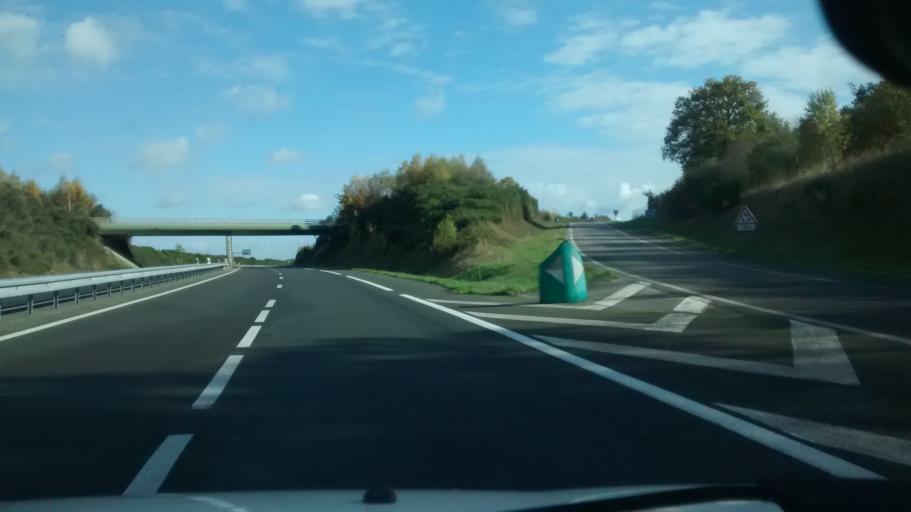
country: FR
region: Pays de la Loire
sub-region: Departement de Maine-et-Loire
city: Noyant-la-Gravoyere
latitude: 47.7074
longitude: -0.9761
